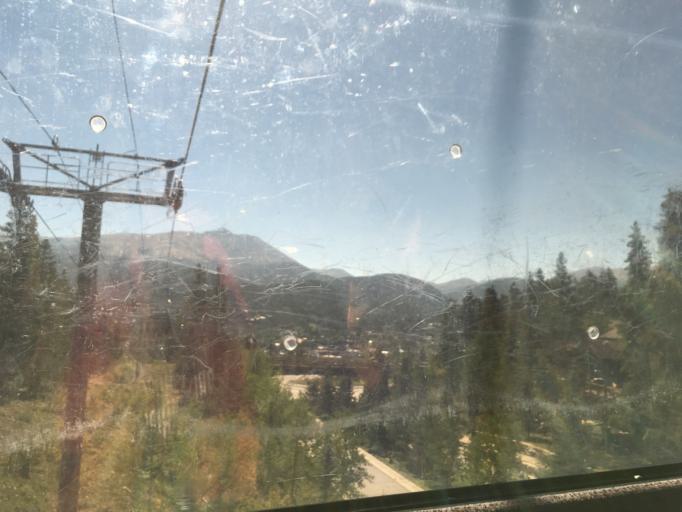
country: US
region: Colorado
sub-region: Summit County
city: Breckenridge
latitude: 39.4877
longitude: -106.0535
